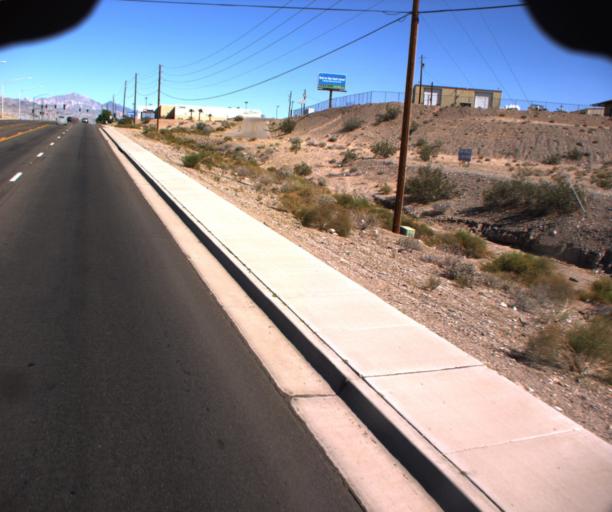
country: US
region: Arizona
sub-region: Mohave County
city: Bullhead City
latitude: 35.0785
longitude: -114.5944
